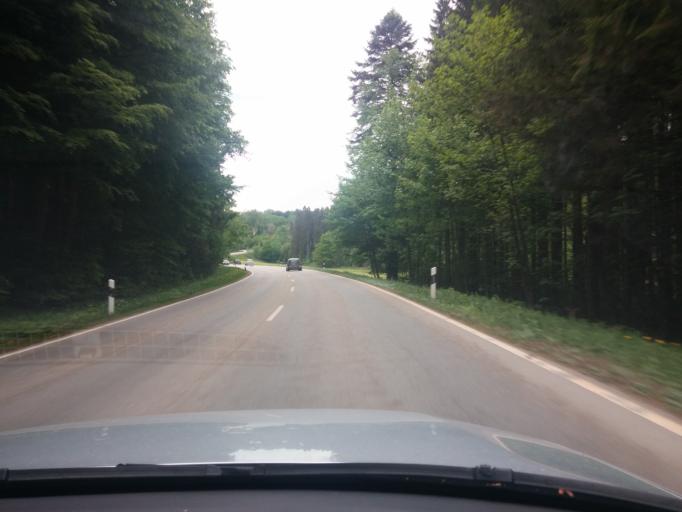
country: DE
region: Bavaria
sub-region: Upper Bavaria
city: Sachsenkam
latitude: 47.8286
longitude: 11.6557
